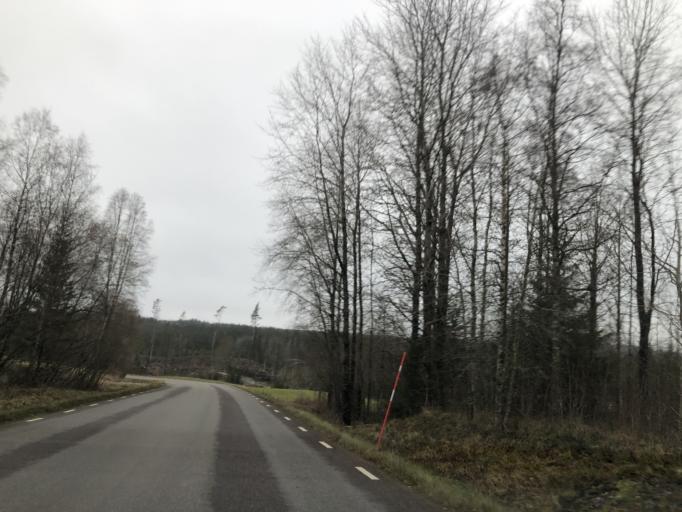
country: SE
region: Vaestra Goetaland
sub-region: Ulricehamns Kommun
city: Ulricehamn
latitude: 57.7679
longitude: 13.4628
